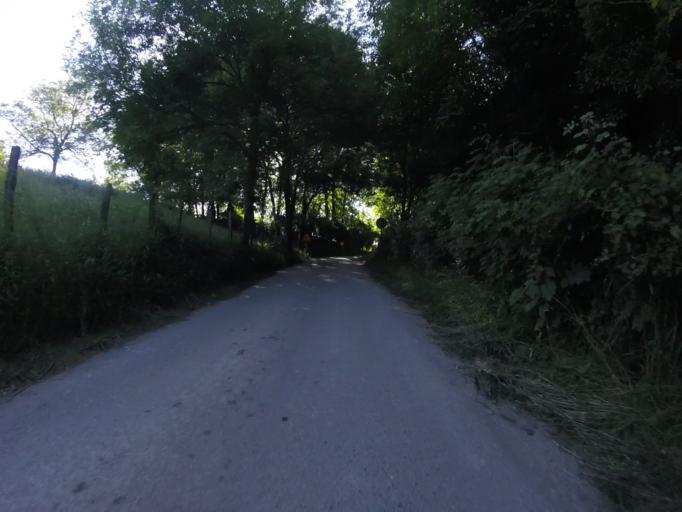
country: ES
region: Basque Country
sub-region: Provincia de Guipuzcoa
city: Astigarraga
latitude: 43.2946
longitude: -1.9317
